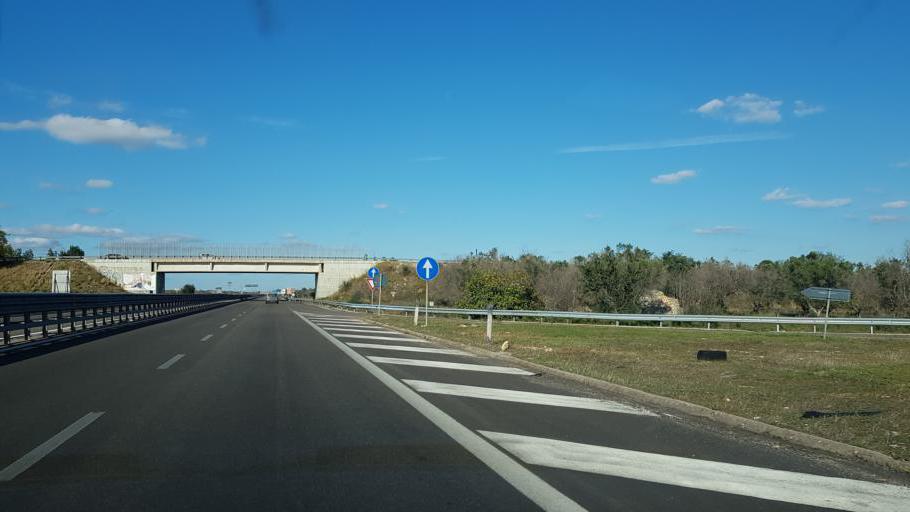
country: IT
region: Apulia
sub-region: Provincia di Lecce
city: Collemeto
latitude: 40.2566
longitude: 18.1182
